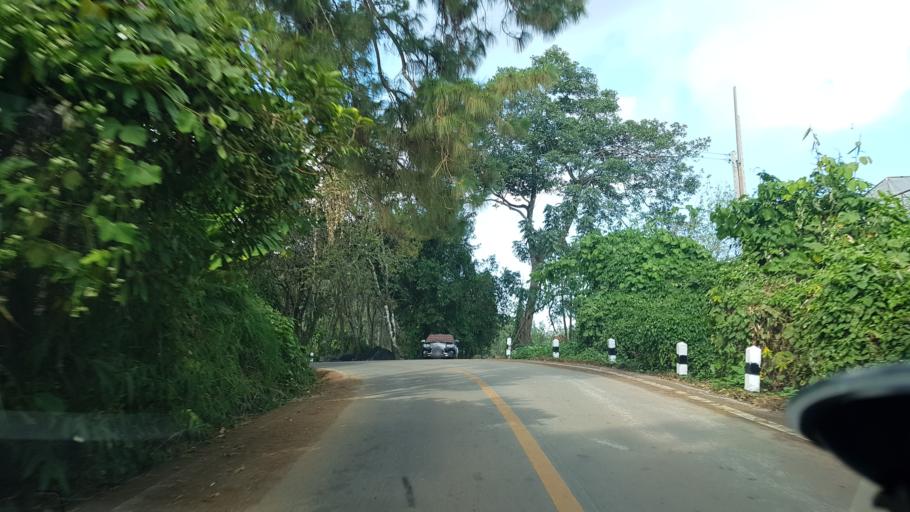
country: TH
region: Chiang Rai
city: Mae Fa Luang
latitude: 20.3276
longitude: 99.8155
